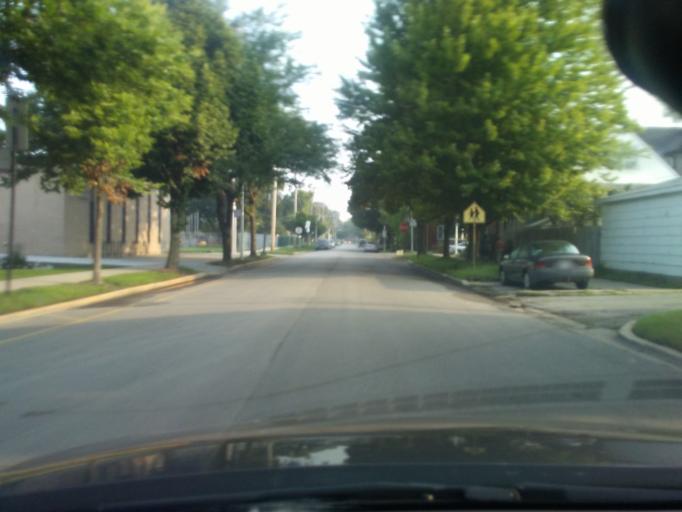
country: US
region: Illinois
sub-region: Cook County
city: Lincolnwood
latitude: 42.0096
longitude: -87.7045
